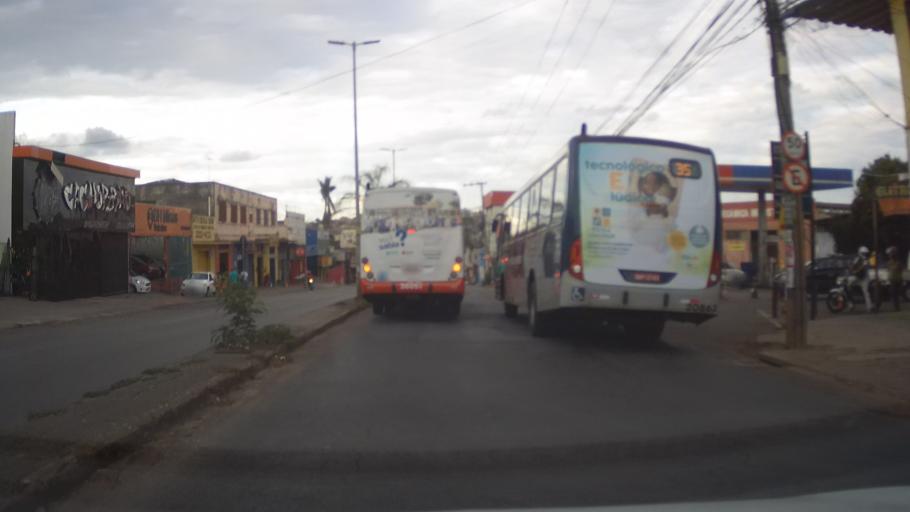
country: BR
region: Minas Gerais
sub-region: Contagem
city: Contagem
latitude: -19.9592
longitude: -44.0161
